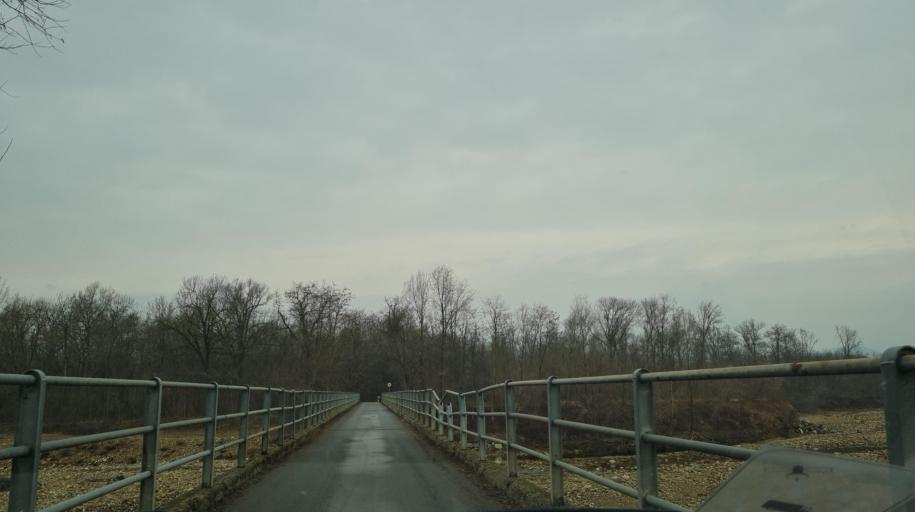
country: IT
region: Piedmont
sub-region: Provincia di Biella
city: Borriana
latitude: 45.5123
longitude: 8.0256
